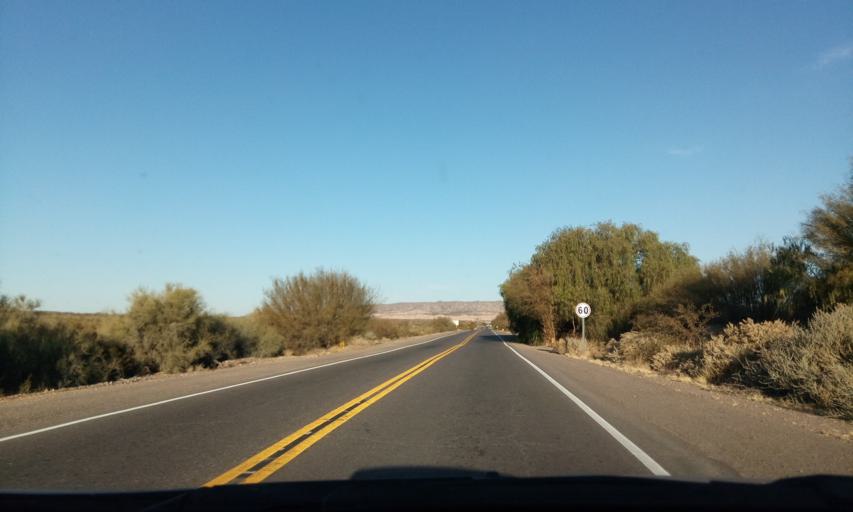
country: AR
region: San Juan
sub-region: Departamento de Rivadavia
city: Rivadavia
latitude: -31.4338
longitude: -68.6614
